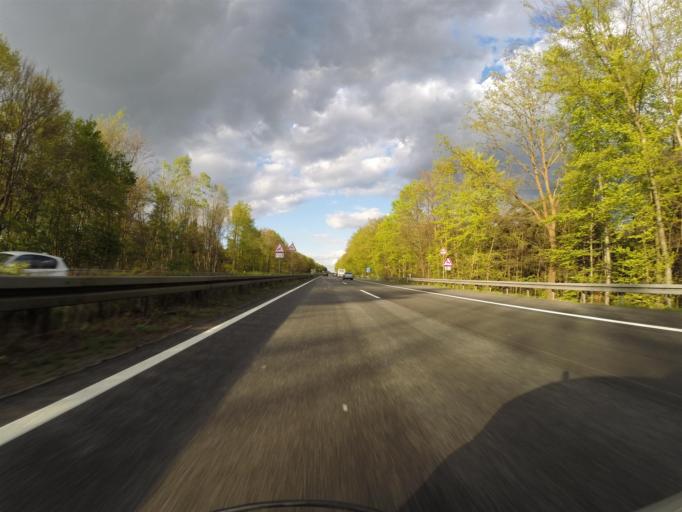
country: DE
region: Saarland
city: Bexbach
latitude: 49.3335
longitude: 7.2850
